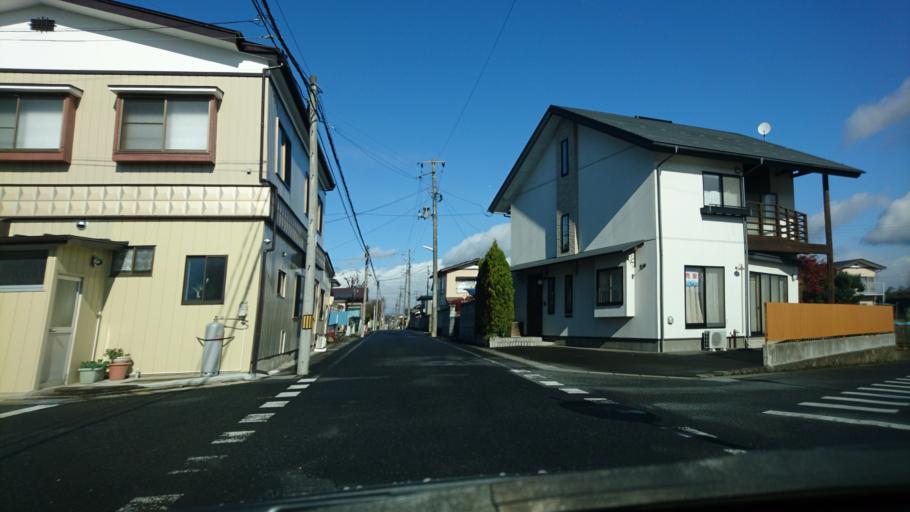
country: JP
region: Iwate
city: Ichinoseki
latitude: 38.9369
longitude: 141.1272
